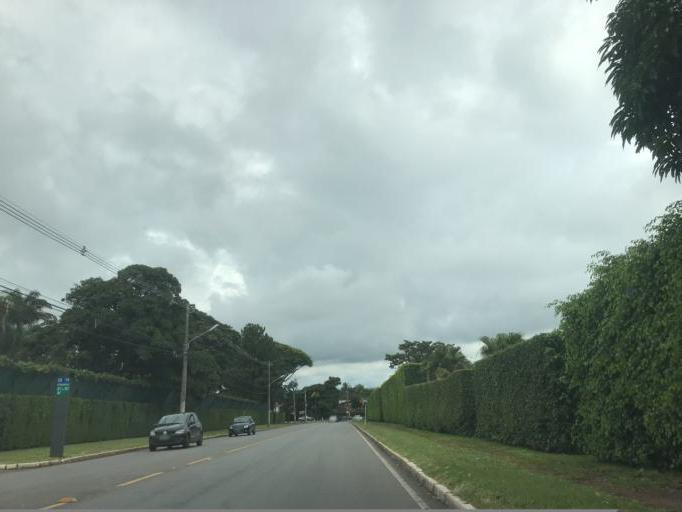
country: BR
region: Federal District
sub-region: Brasilia
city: Brasilia
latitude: -15.8479
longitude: -47.8858
